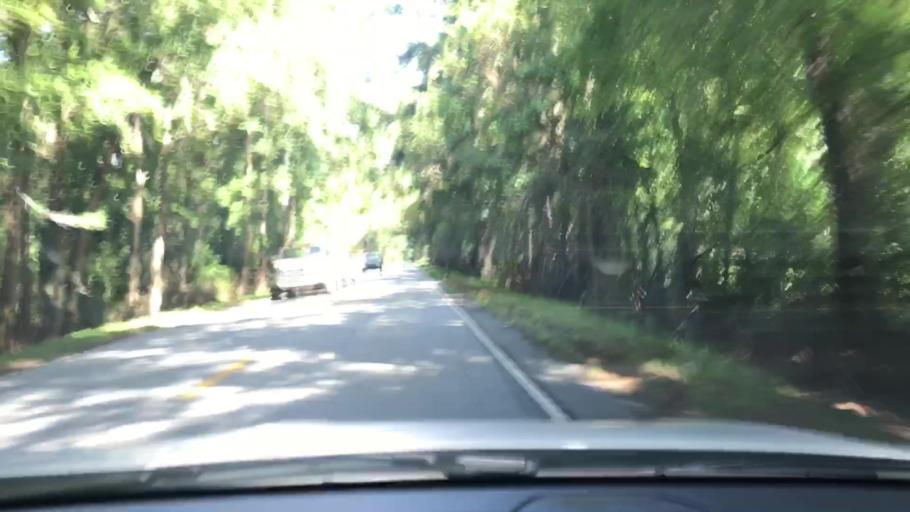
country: US
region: South Carolina
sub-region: Berkeley County
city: Ladson
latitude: 32.8927
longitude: -80.1316
